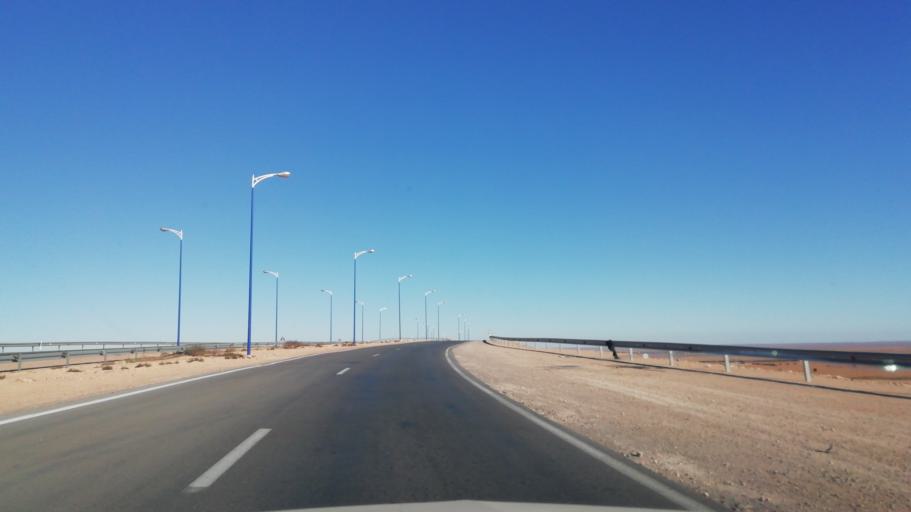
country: DZ
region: Wilaya de Naama
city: Naama
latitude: 33.5125
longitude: -0.2830
